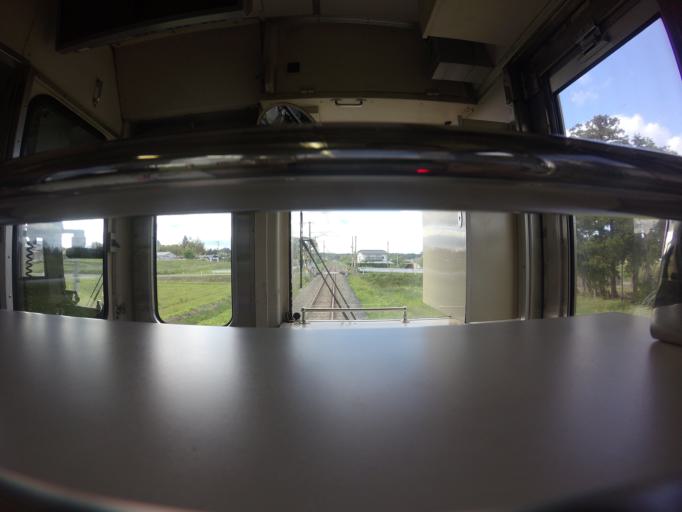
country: JP
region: Fukushima
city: Namie
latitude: 37.5982
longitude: 140.9967
